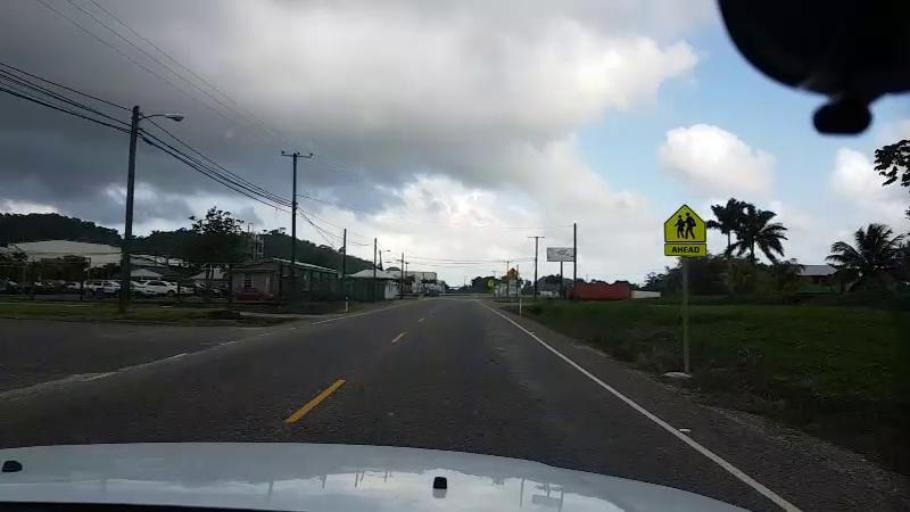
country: BZ
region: Stann Creek
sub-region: Dangriga
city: Dangriga
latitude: 16.9936
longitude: -88.3735
